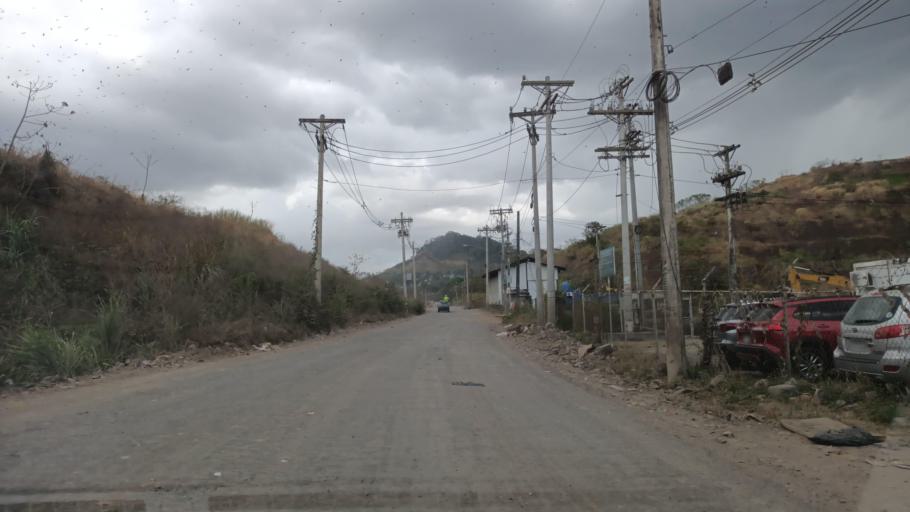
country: PA
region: Panama
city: Las Cumbres
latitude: 9.0536
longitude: -79.5676
